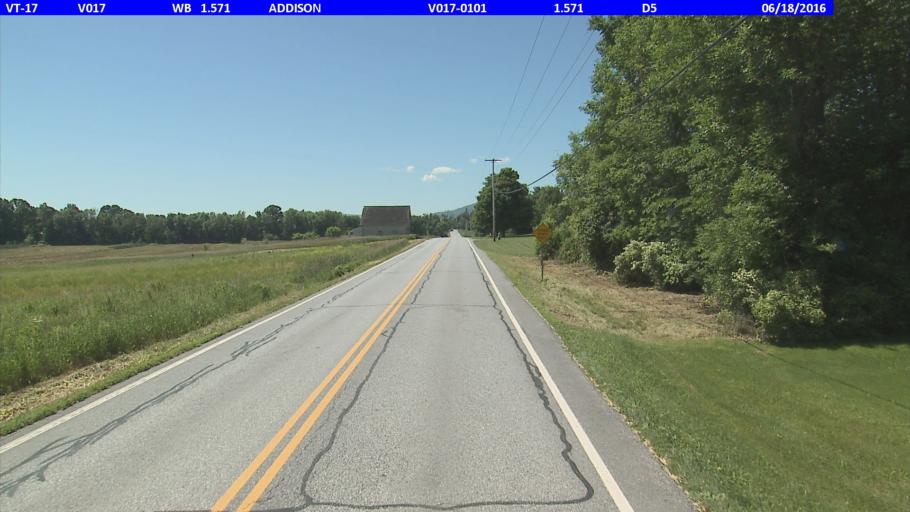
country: US
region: New York
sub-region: Essex County
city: Port Henry
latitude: 44.0525
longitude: -73.4128
